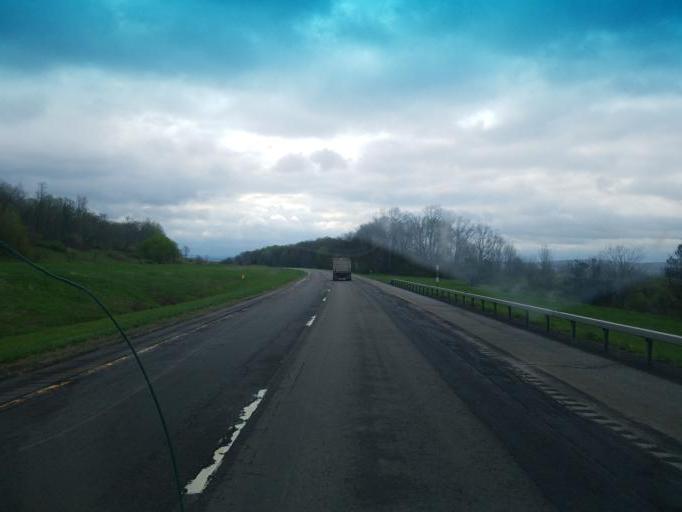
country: US
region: New York
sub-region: Chautauqua County
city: Lakewood
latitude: 42.1308
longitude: -79.3263
